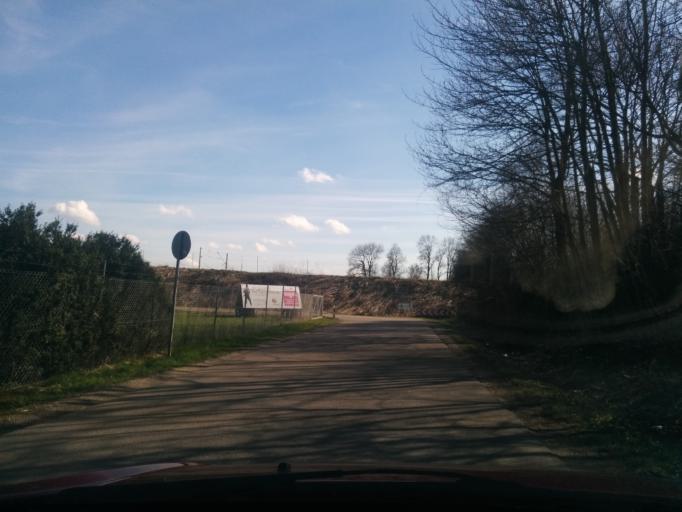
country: DE
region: Bavaria
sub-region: Upper Bavaria
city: Karlsfeld
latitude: 48.2052
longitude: 11.4323
